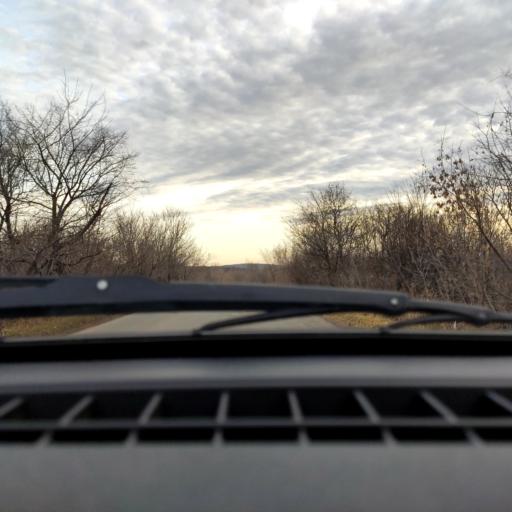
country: RU
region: Bashkortostan
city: Ufa
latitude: 54.8721
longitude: 56.1318
